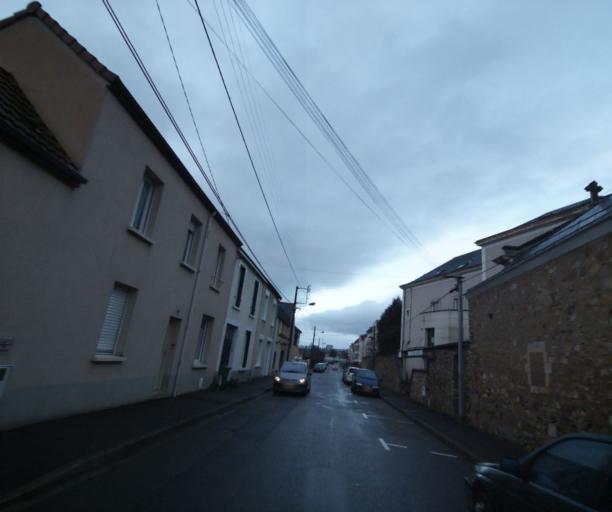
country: FR
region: Pays de la Loire
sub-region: Departement de la Sarthe
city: Coulaines
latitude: 48.0138
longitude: 0.1947
